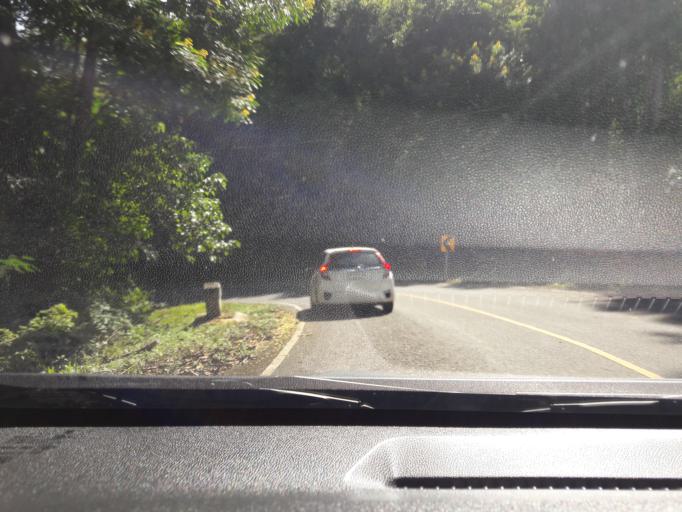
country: TH
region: Mae Hong Son
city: Sop Pong
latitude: 19.5717
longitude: 98.2004
